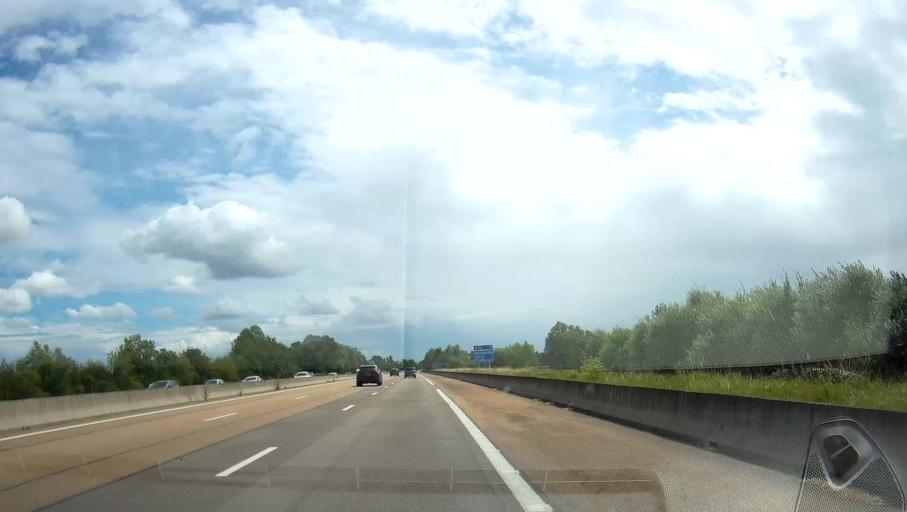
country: FR
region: Bourgogne
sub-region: Departement de la Cote-d'Or
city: Couternon
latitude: 47.3373
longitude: 5.1659
